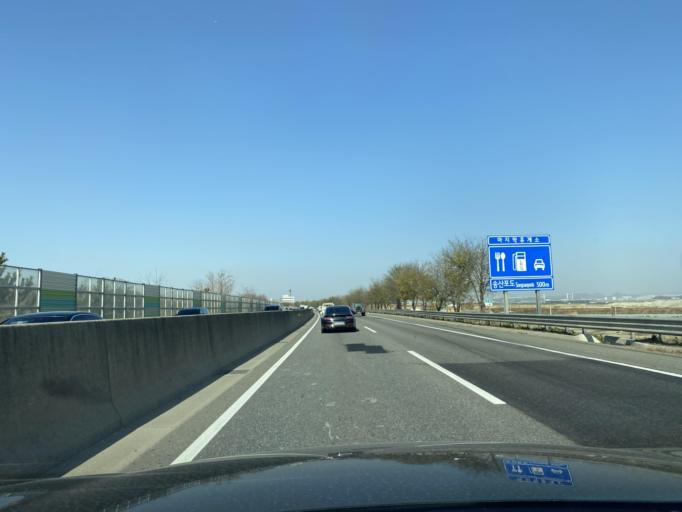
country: KR
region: Gyeonggi-do
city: Hwaseong-si
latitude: 37.2283
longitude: 126.7611
